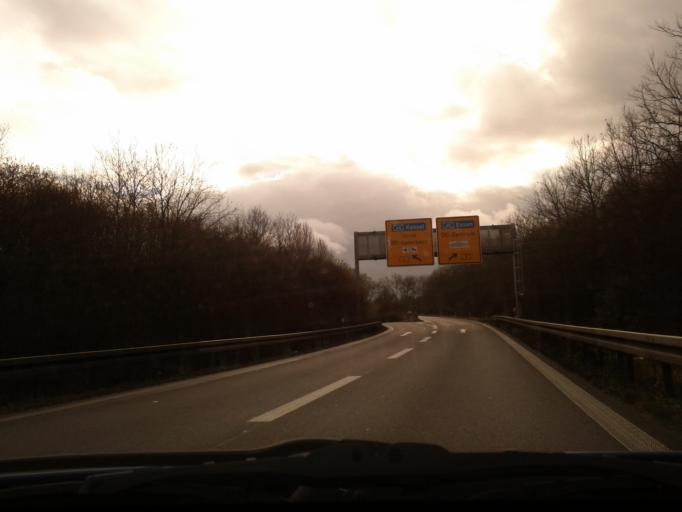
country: DE
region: North Rhine-Westphalia
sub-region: Regierungsbezirk Arnsberg
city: Dortmund
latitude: 51.5082
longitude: 7.5224
